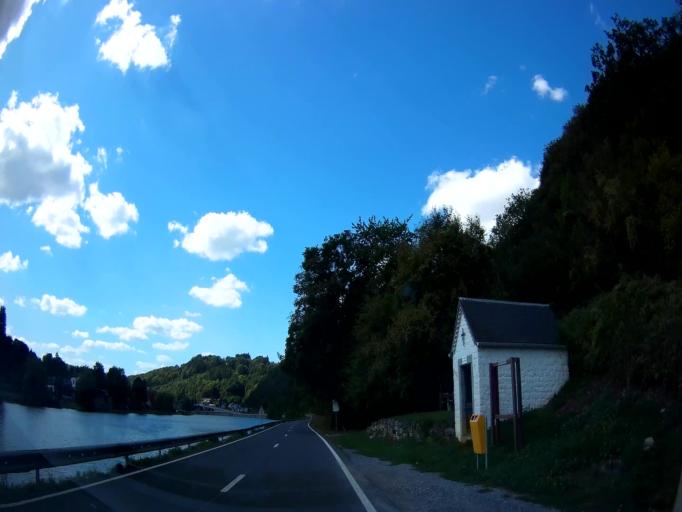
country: BE
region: Wallonia
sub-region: Province de Namur
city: Hastiere-Lavaux
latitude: 50.2168
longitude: 4.8369
